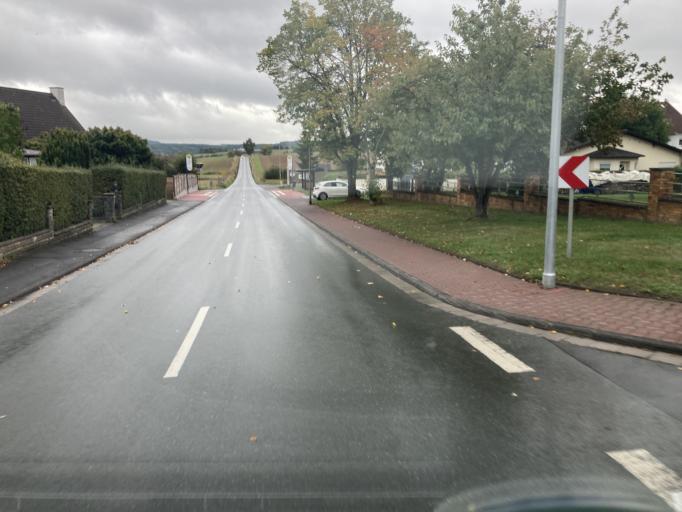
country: DE
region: Hesse
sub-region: Regierungsbezirk Darmstadt
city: Usingen
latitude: 50.3517
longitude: 8.5365
